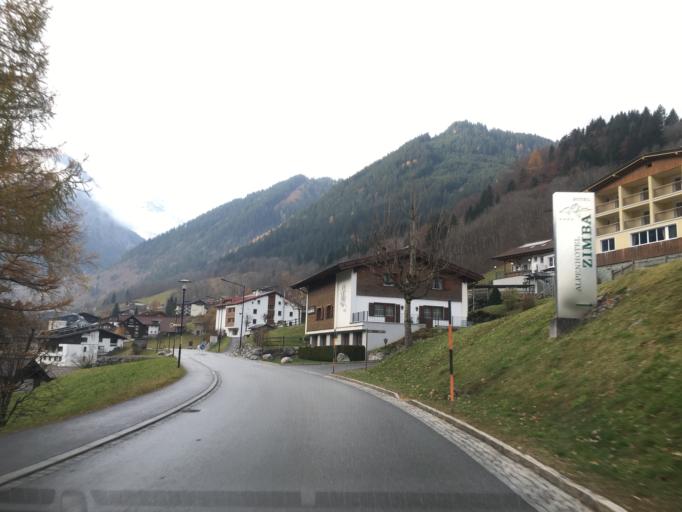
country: AT
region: Vorarlberg
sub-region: Politischer Bezirk Bludenz
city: Brand
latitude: 47.1145
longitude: 9.7478
